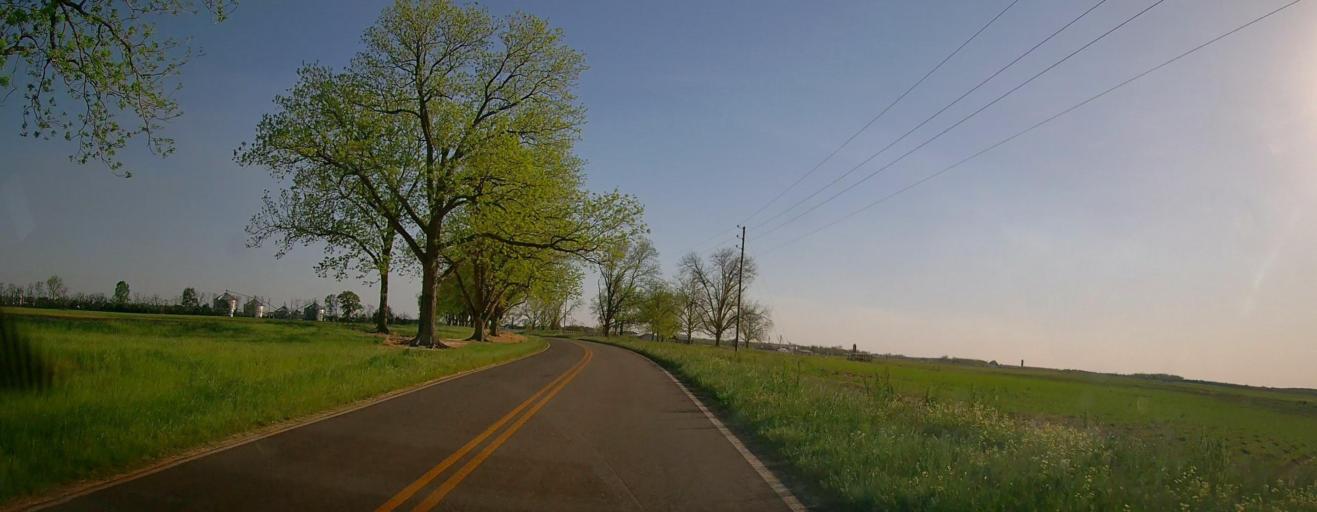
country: US
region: Georgia
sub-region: Macon County
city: Montezuma
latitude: 32.3296
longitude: -83.9619
